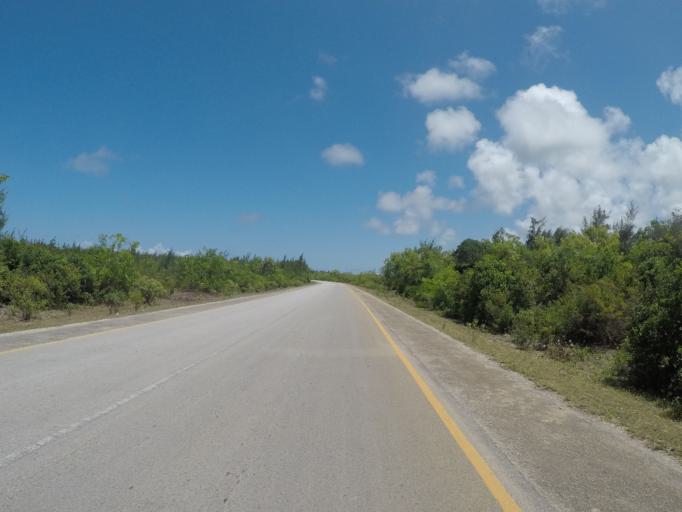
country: TZ
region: Zanzibar Central/South
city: Nganane
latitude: -6.3889
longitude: 39.5590
